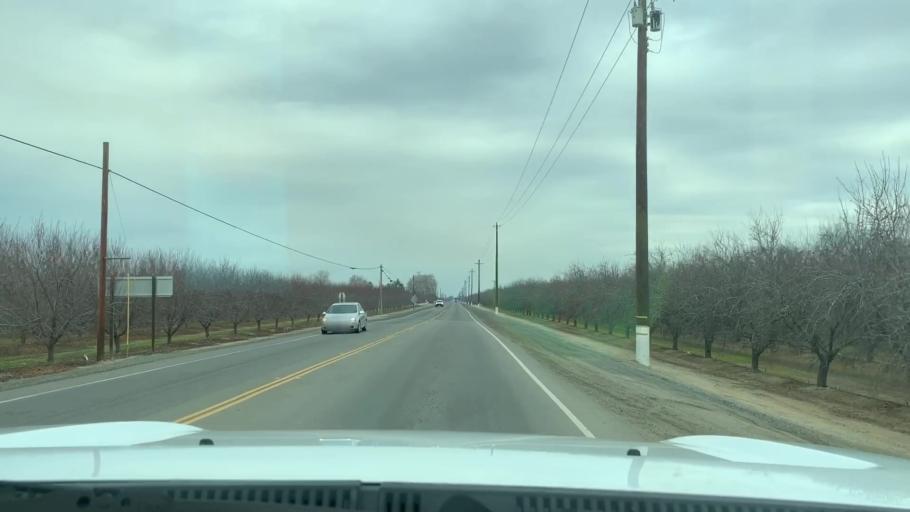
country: US
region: California
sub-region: Kern County
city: Shafter
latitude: 35.3988
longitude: -119.2520
